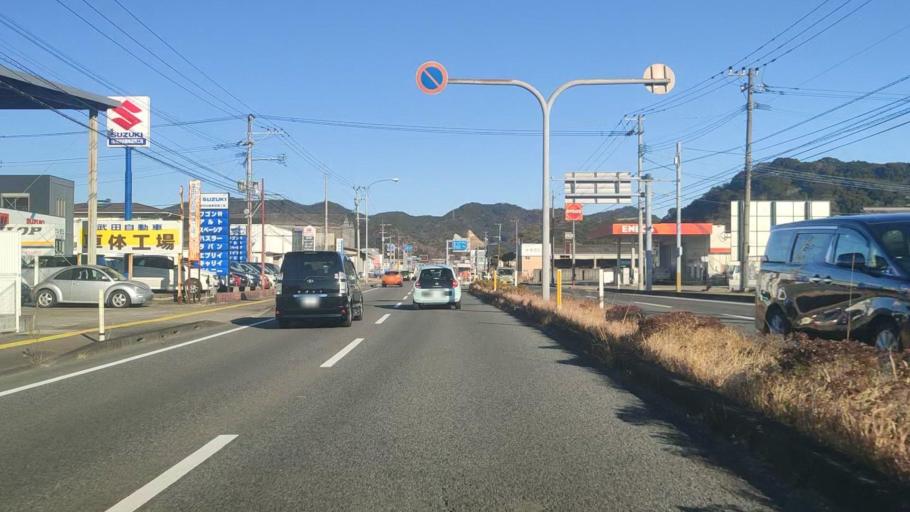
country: JP
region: Miyazaki
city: Nobeoka
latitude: 32.4894
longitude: 131.6642
